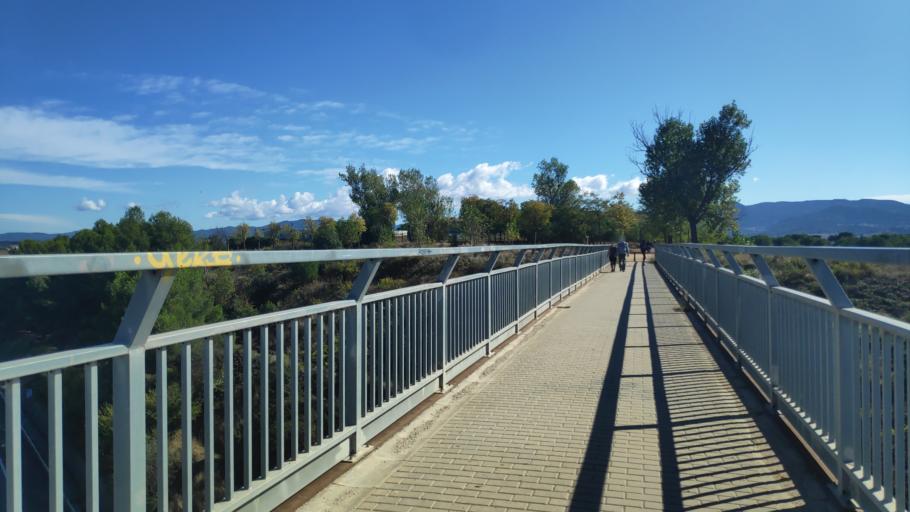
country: ES
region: Catalonia
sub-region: Provincia de Barcelona
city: Santa Perpetua de Mogoda
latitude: 41.5459
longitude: 2.1959
